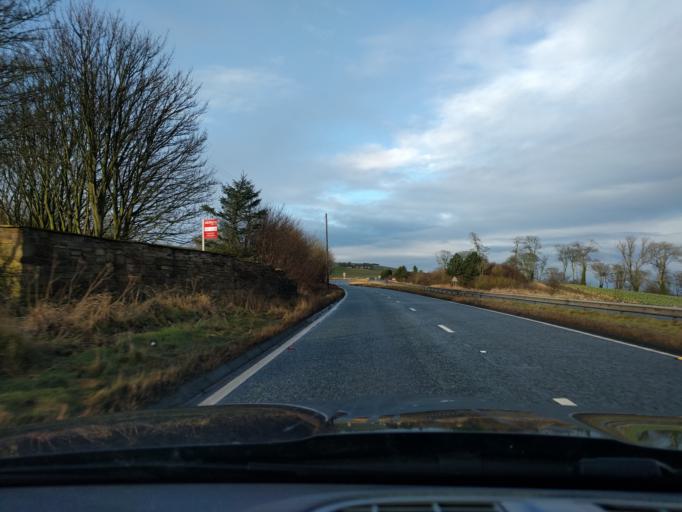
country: GB
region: England
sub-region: Northumberland
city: Berwick-Upon-Tweed
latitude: 55.7987
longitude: -2.0349
